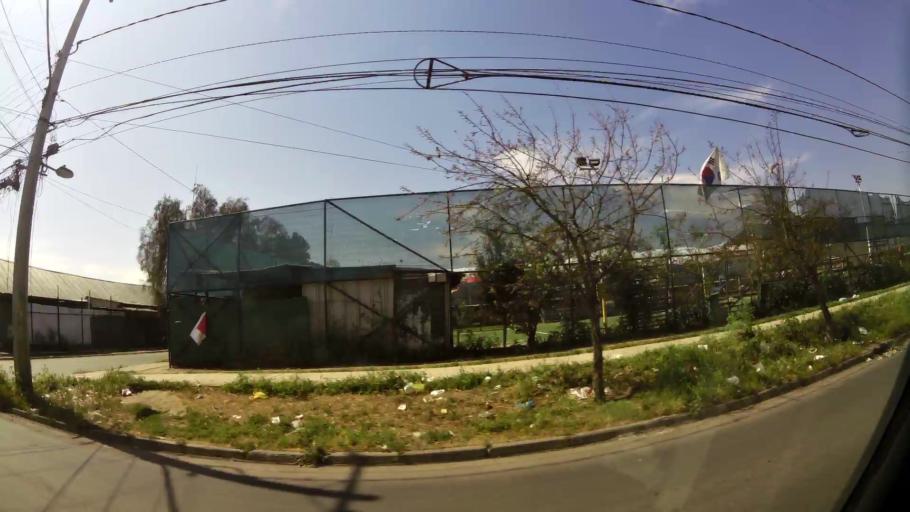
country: CL
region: Santiago Metropolitan
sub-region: Provincia de Santiago
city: Lo Prado
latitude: -33.4720
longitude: -70.7071
